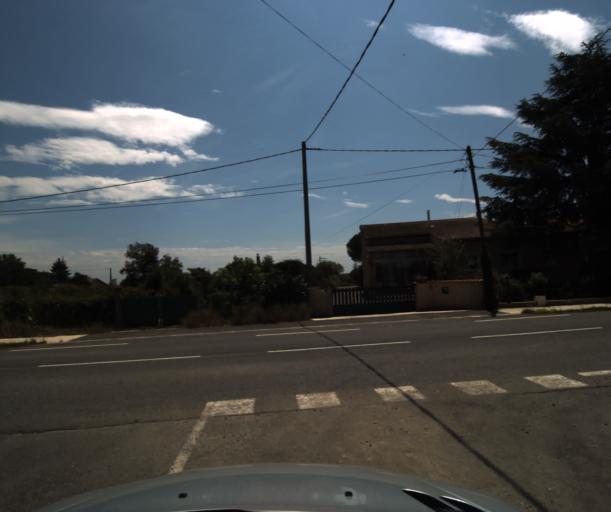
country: FR
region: Midi-Pyrenees
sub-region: Departement de la Haute-Garonne
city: Labastidette
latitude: 43.4678
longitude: 1.2398
